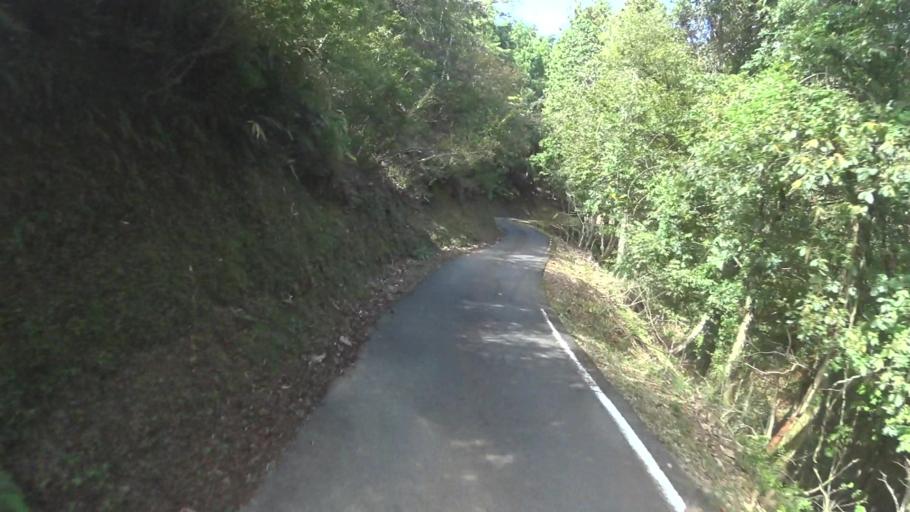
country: JP
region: Hyogo
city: Toyooka
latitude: 35.6055
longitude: 134.9964
